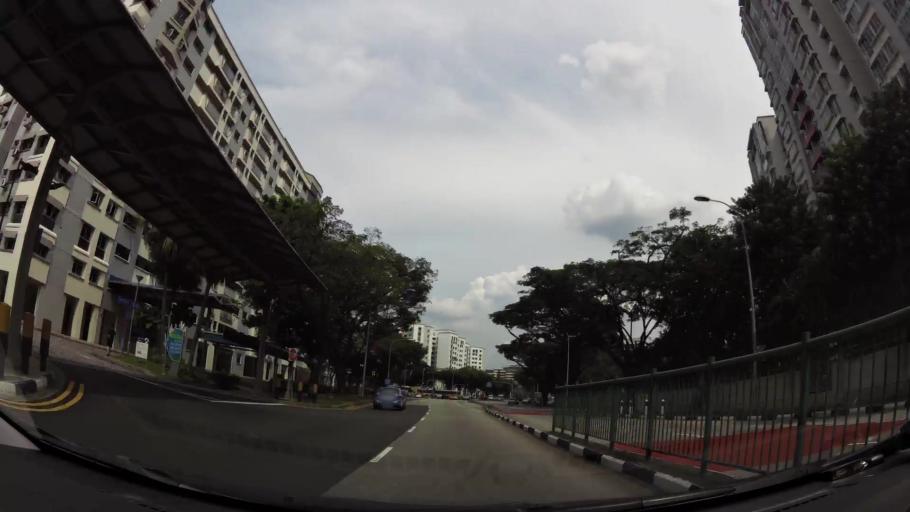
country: MY
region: Johor
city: Johor Bahru
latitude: 1.4319
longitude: 103.7865
